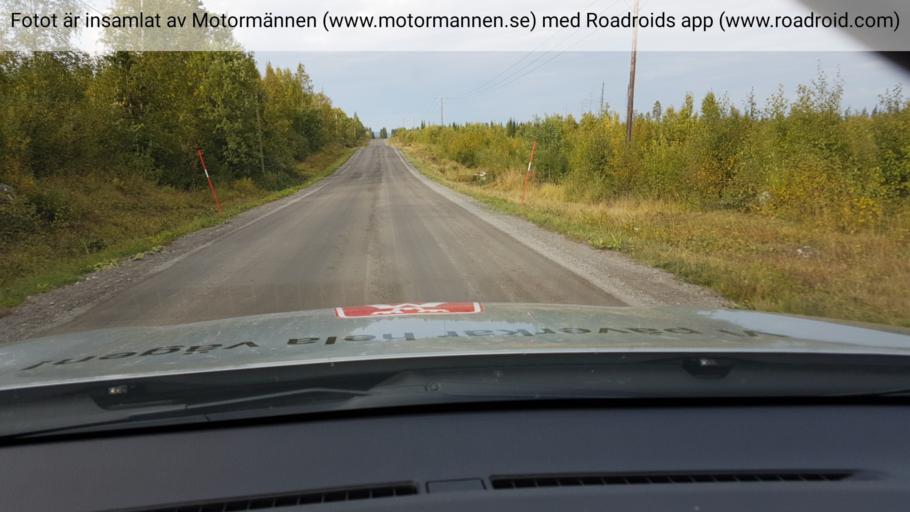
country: SE
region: Jaemtland
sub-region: Stroemsunds Kommun
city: Stroemsund
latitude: 63.9902
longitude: 15.8165
